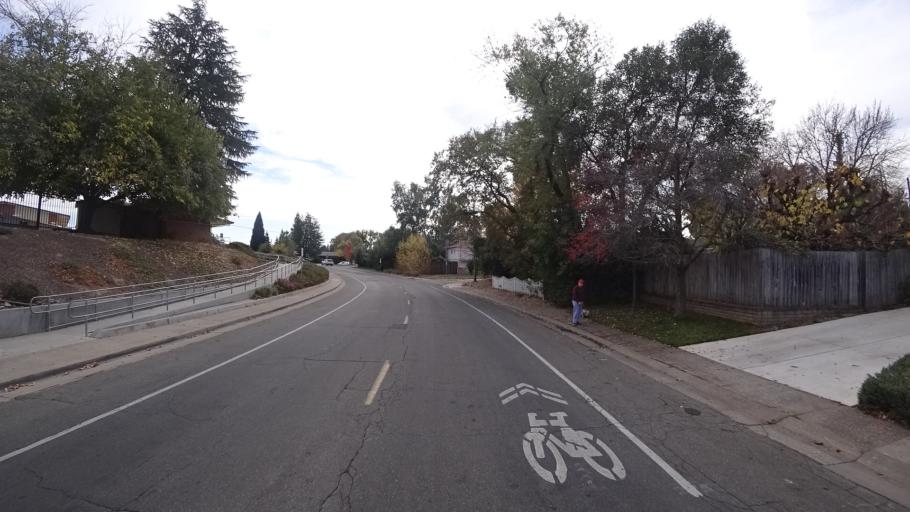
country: US
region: California
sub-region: Sacramento County
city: Fair Oaks
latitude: 38.6705
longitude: -121.2785
